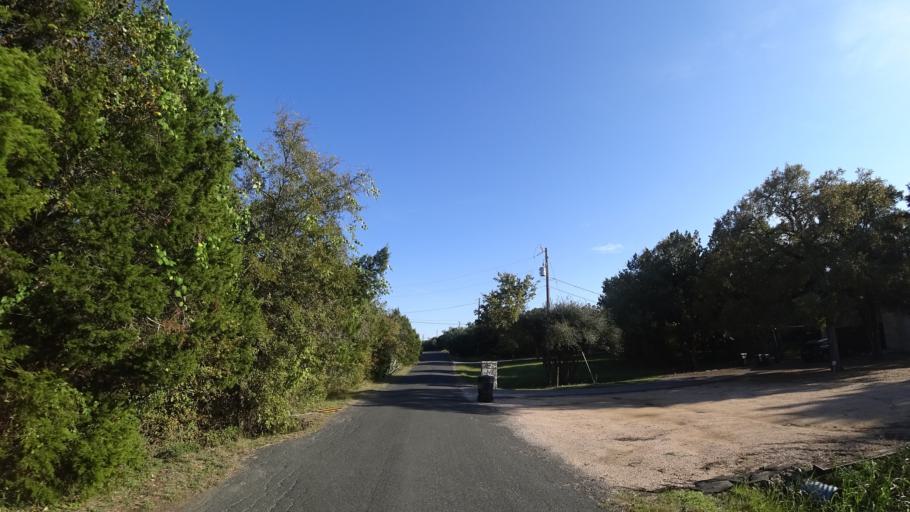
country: US
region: Texas
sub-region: Travis County
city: Barton Creek
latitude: 30.2436
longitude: -97.9131
